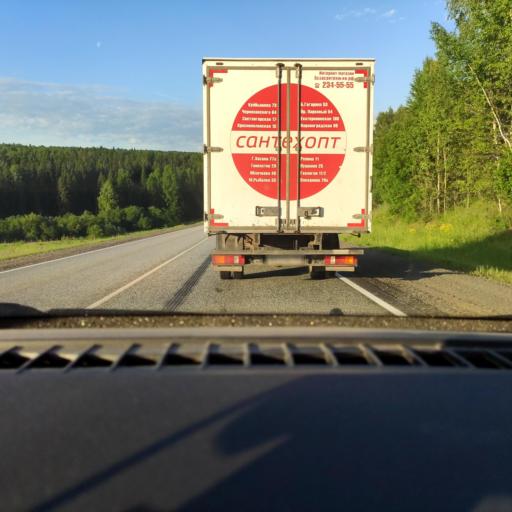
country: RU
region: Perm
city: Pavlovskiy
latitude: 57.9005
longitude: 54.9514
